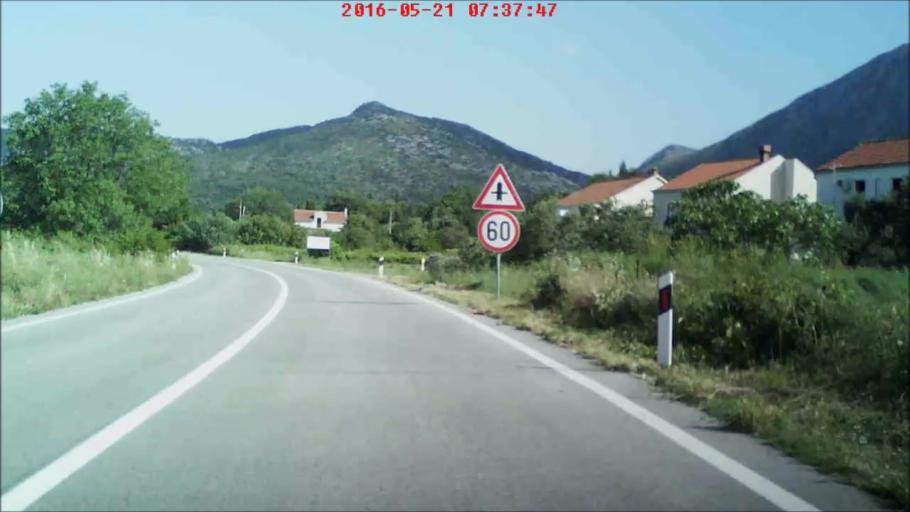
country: HR
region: Dubrovacko-Neretvanska
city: Podgora
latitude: 42.7951
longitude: 17.8542
